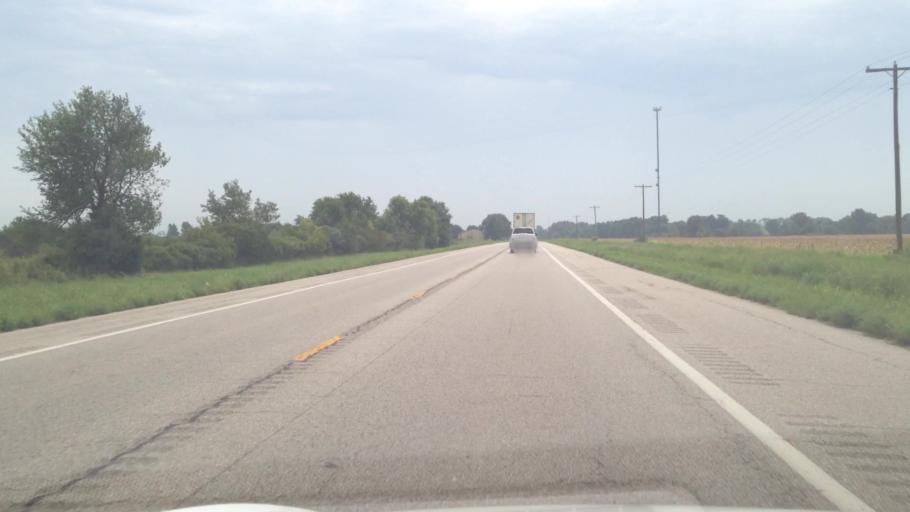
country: US
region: Missouri
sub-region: Jasper County
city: Carl Junction
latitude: 37.2131
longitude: -94.7049
